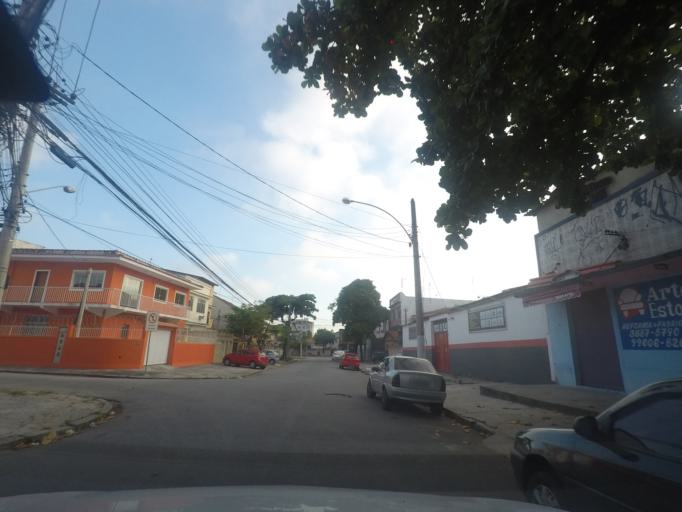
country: BR
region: Rio de Janeiro
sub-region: Duque De Caxias
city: Duque de Caxias
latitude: -22.8347
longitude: -43.2787
